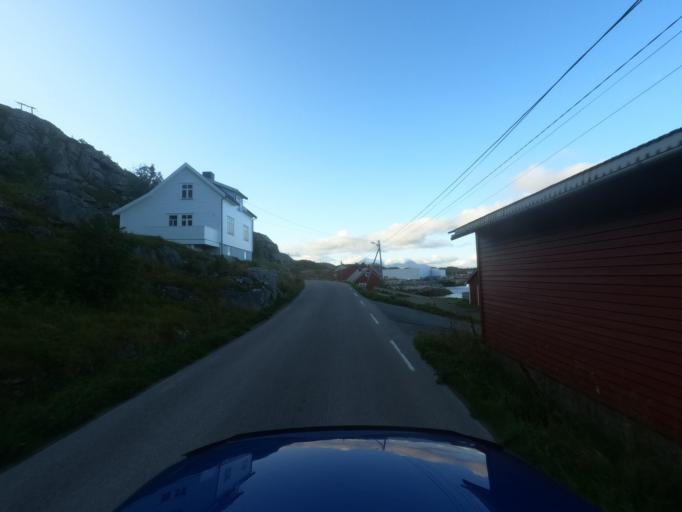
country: NO
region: Nordland
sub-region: Vestvagoy
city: Gravdal
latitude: 68.0733
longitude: 13.5285
